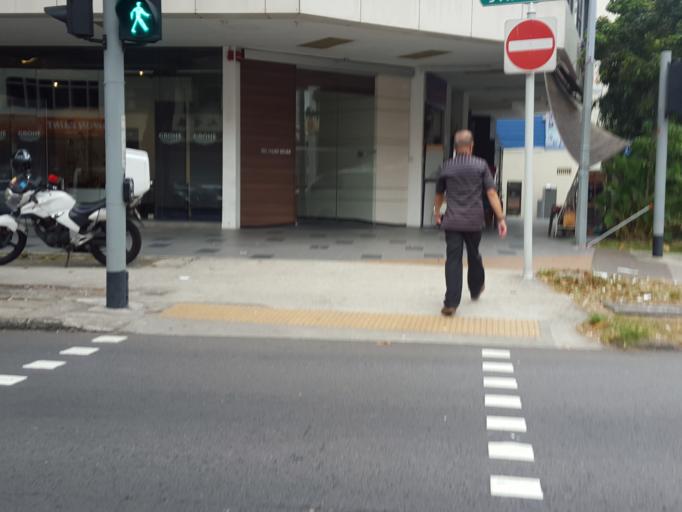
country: SG
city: Singapore
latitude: 1.3114
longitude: 103.8592
